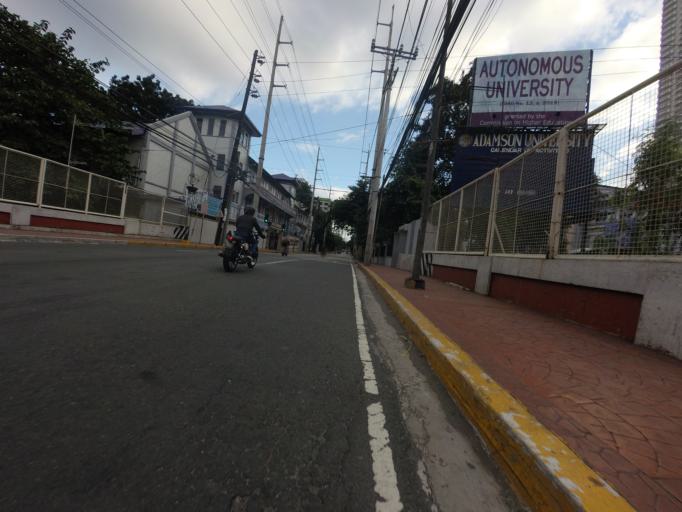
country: PH
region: Metro Manila
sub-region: City of Manila
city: Quiapo
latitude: 14.5864
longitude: 120.9856
